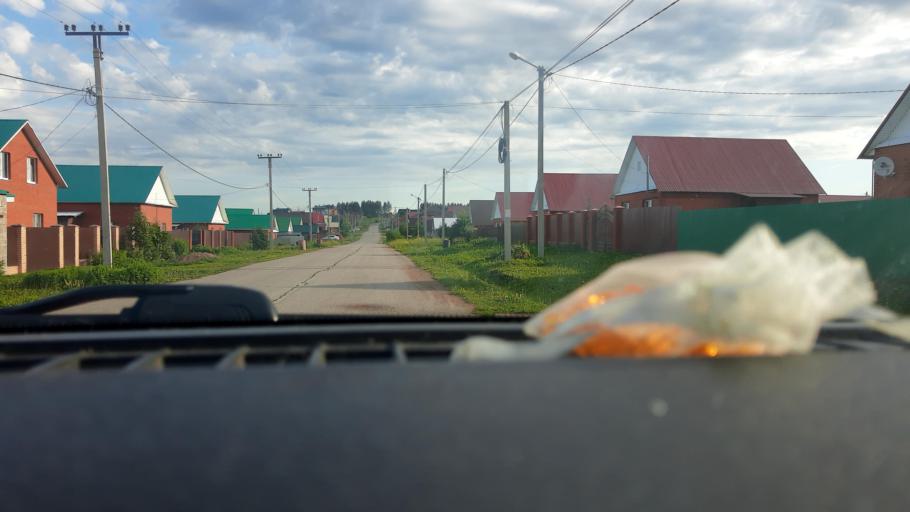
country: RU
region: Bashkortostan
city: Kabakovo
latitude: 54.6627
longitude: 56.2158
